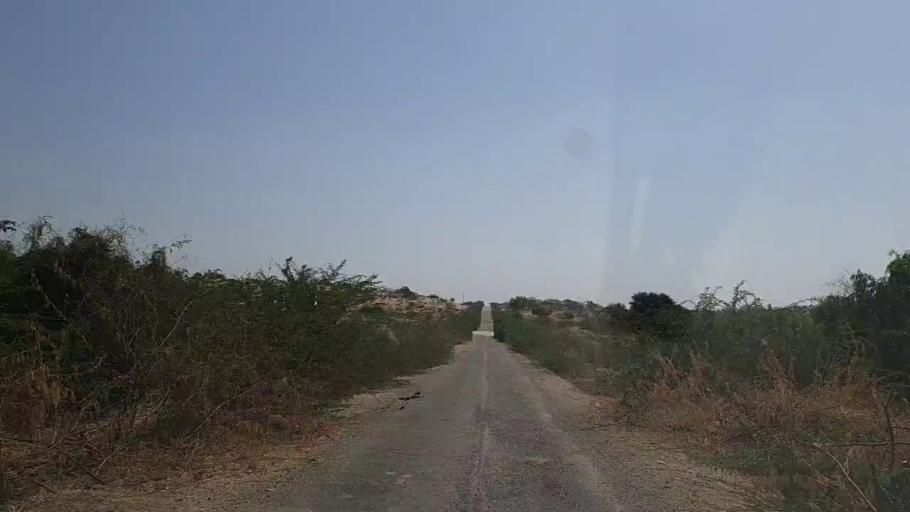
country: PK
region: Sindh
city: Diplo
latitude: 24.4987
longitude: 69.4300
